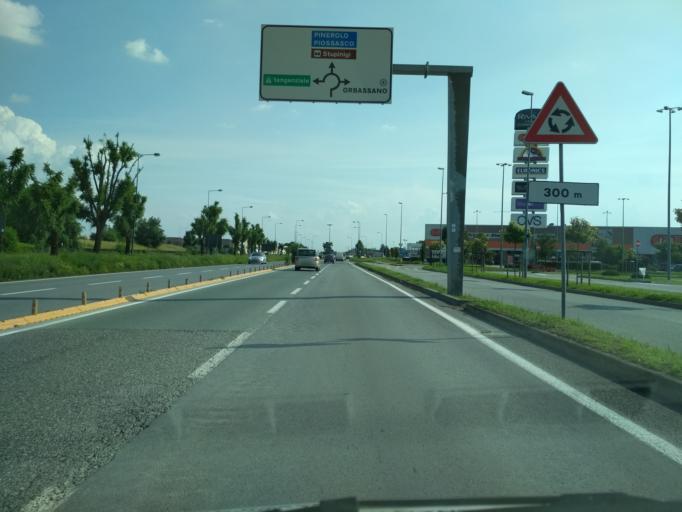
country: IT
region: Piedmont
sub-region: Provincia di Torino
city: Pasta
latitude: 45.0091
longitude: 7.5553
